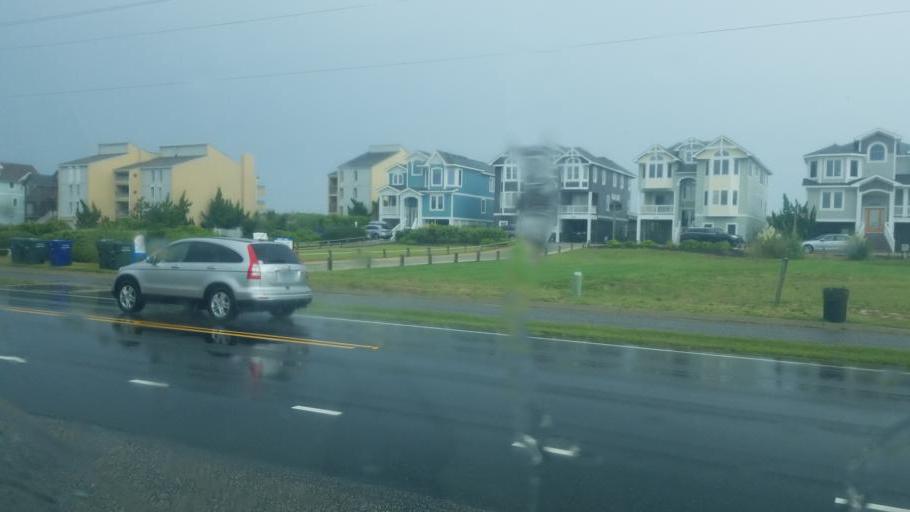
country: US
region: North Carolina
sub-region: Dare County
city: Nags Head
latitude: 35.9901
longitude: -75.6431
